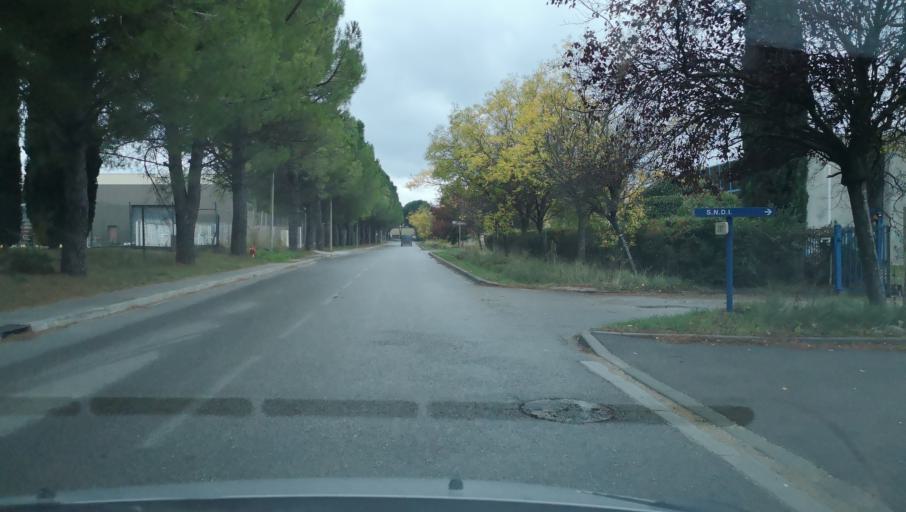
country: FR
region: Provence-Alpes-Cote d'Azur
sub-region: Departement des Bouches-du-Rhone
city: Rousset
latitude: 43.4717
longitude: 5.6089
